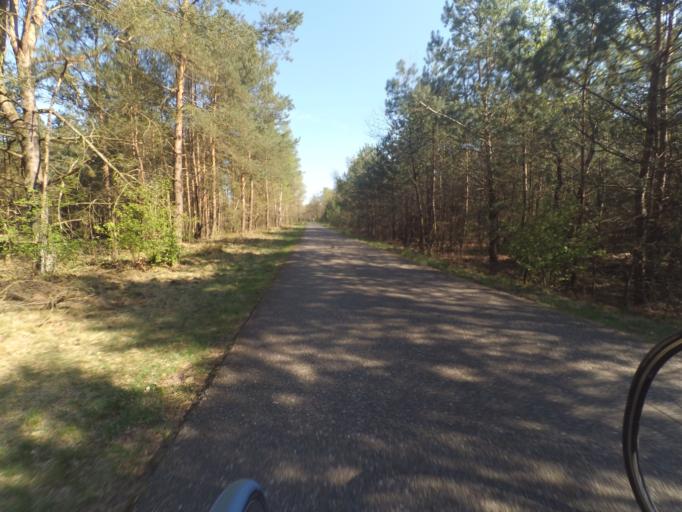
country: NL
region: Gelderland
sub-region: Gemeente Ede
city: Harskamp
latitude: 52.1807
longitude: 5.8148
